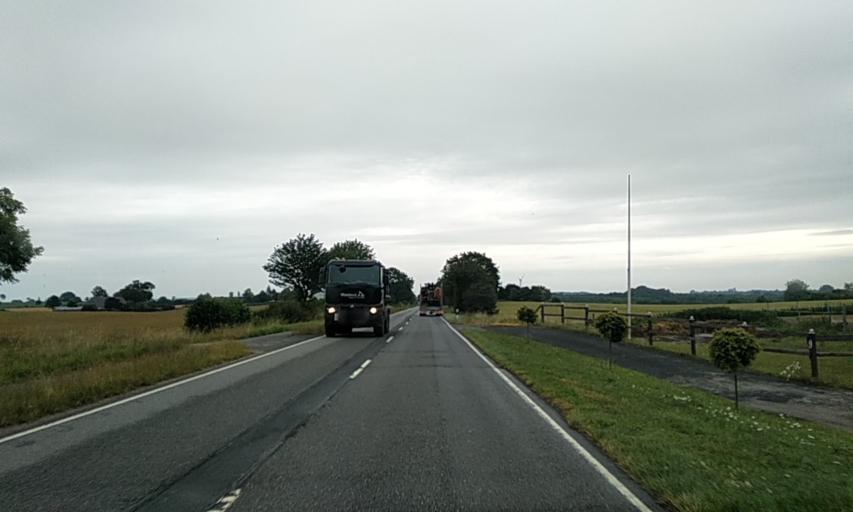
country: DE
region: Schleswig-Holstein
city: Loit
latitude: 54.6366
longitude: 9.6822
